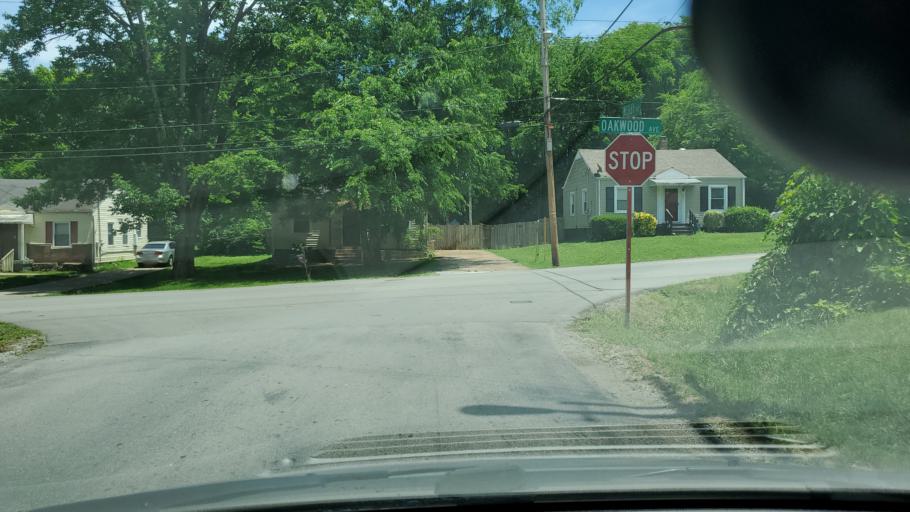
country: US
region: Tennessee
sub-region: Davidson County
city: Nashville
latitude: 36.2060
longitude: -86.7527
